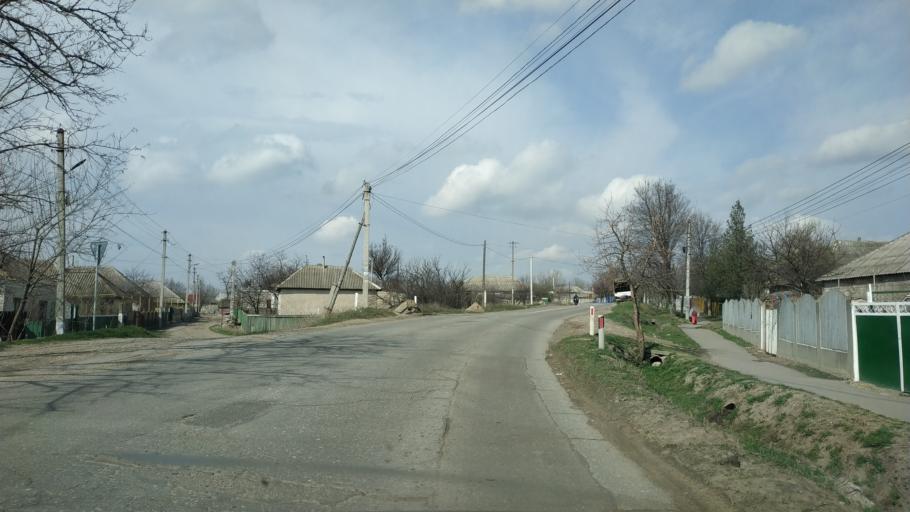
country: MD
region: Gagauzia
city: Vulcanesti
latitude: 45.6918
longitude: 28.4048
